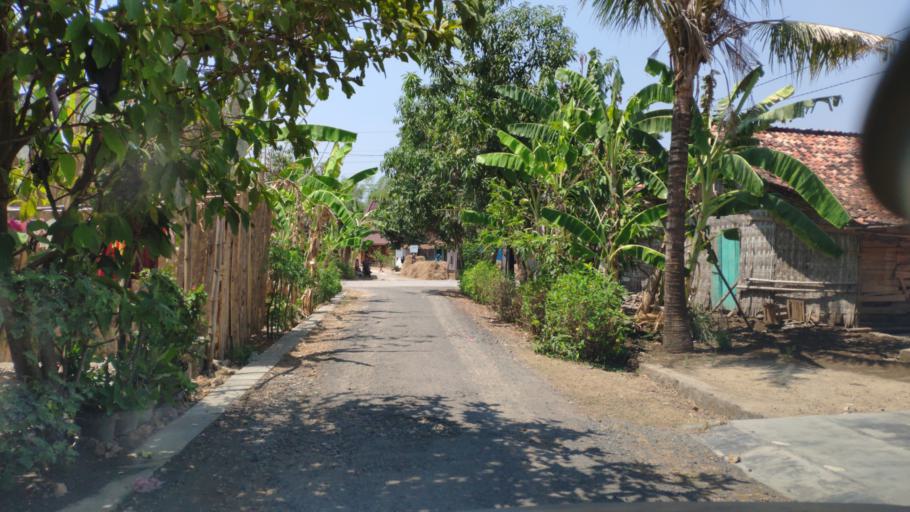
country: ID
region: Central Java
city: Kalirejo
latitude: -6.9195
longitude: 111.4347
